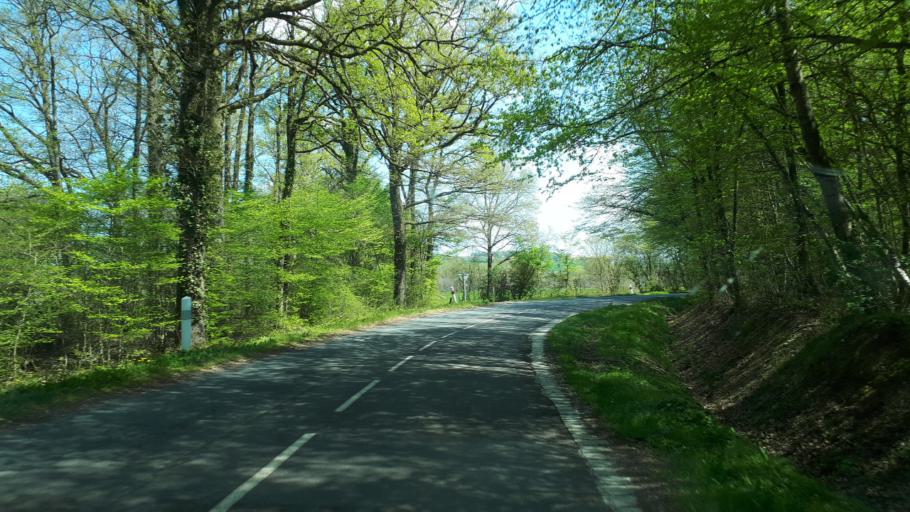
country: FR
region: Centre
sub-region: Departement du Cher
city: Sancerre
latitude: 47.3049
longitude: 2.7021
